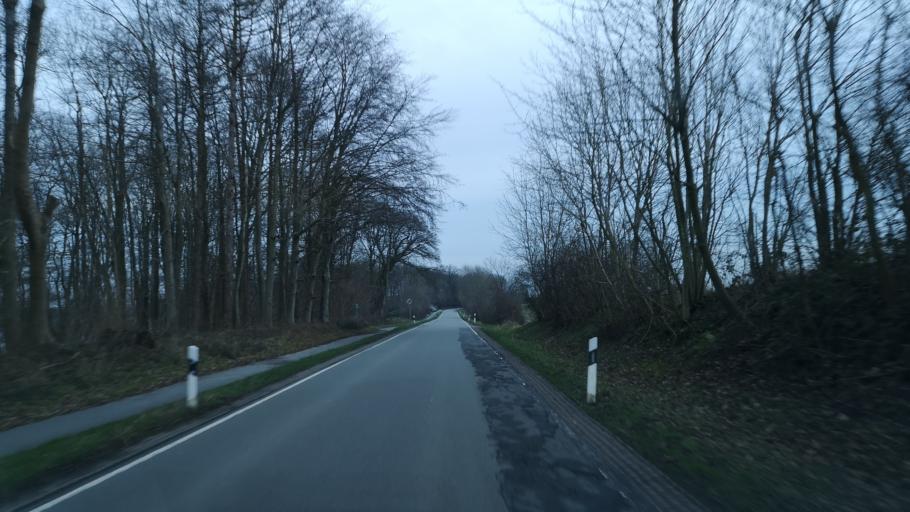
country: DE
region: Schleswig-Holstein
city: Sorup
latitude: 54.7033
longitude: 9.6414
